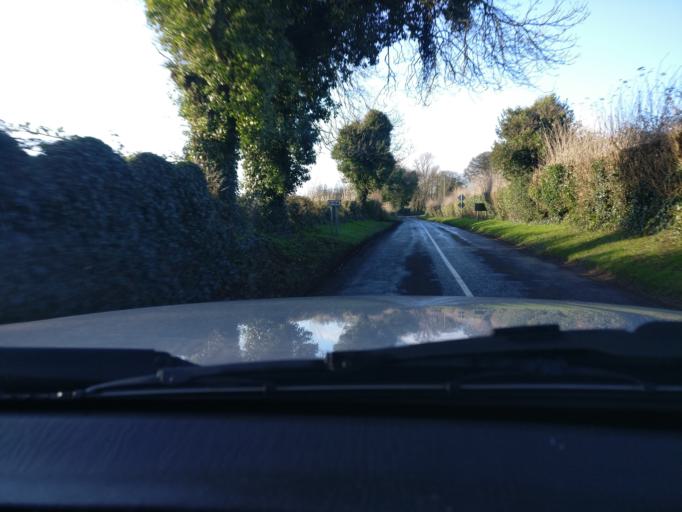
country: IE
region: Leinster
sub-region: An Mhi
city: Athboy
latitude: 53.6936
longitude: -6.9981
